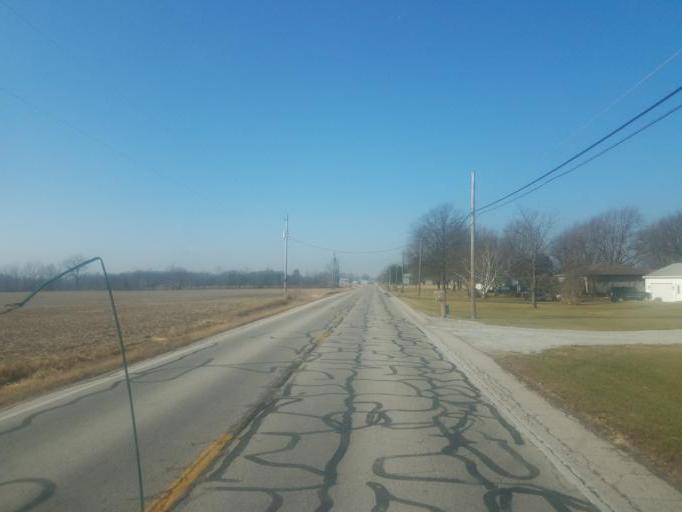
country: US
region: Ohio
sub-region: Seneca County
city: Tiffin
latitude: 41.1243
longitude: -83.1332
